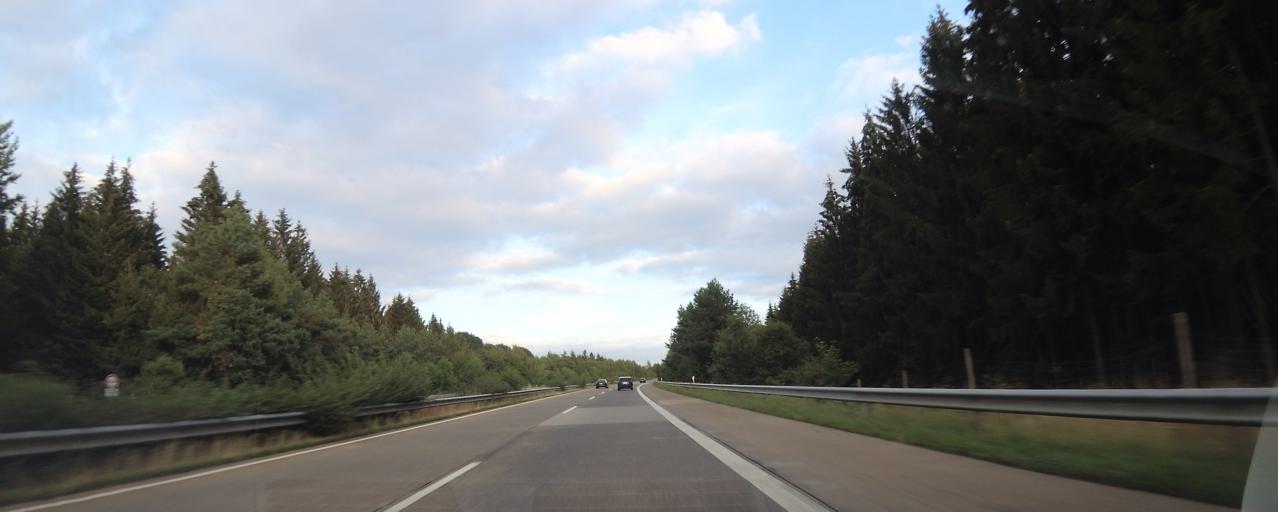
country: DE
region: Rheinland-Pfalz
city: Bescheid
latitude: 49.7393
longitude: 6.8830
